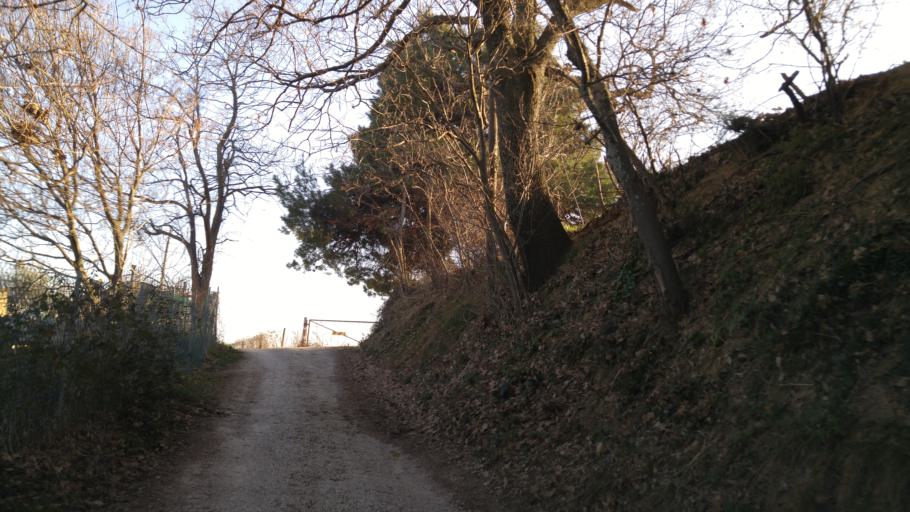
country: IT
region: The Marches
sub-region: Provincia di Pesaro e Urbino
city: Fenile
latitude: 43.8551
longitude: 12.9601
